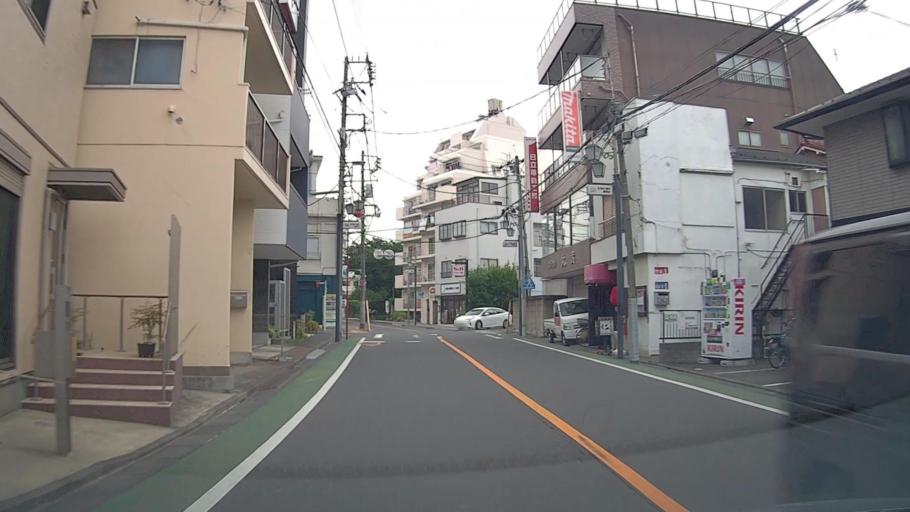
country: JP
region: Saitama
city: Kawaguchi
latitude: 35.7623
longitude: 139.6991
